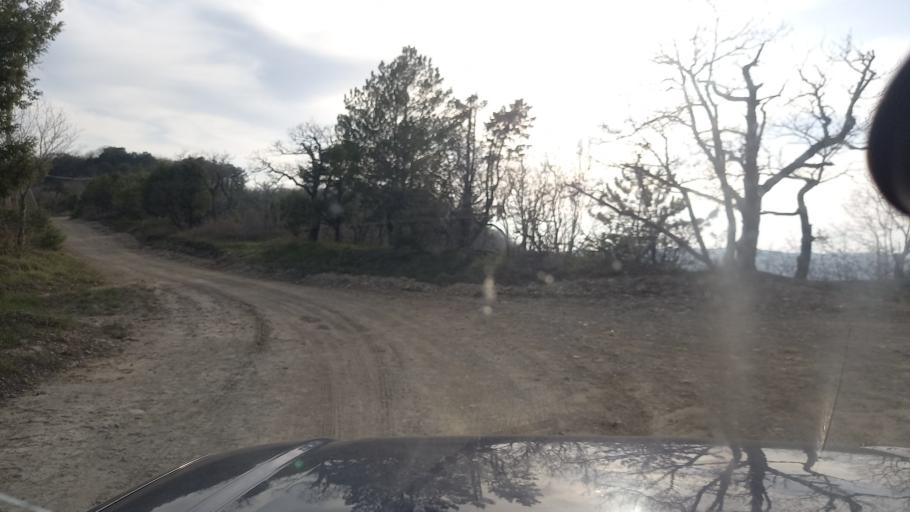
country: RU
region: Krasnodarskiy
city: Arkhipo-Osipovka
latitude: 44.3662
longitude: 38.5787
